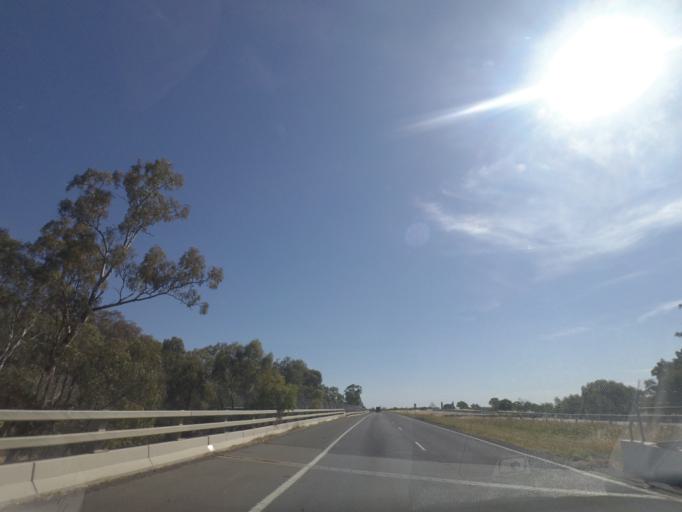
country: AU
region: Victoria
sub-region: Greater Shepparton
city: Shepparton
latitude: -36.6183
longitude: 145.3087
